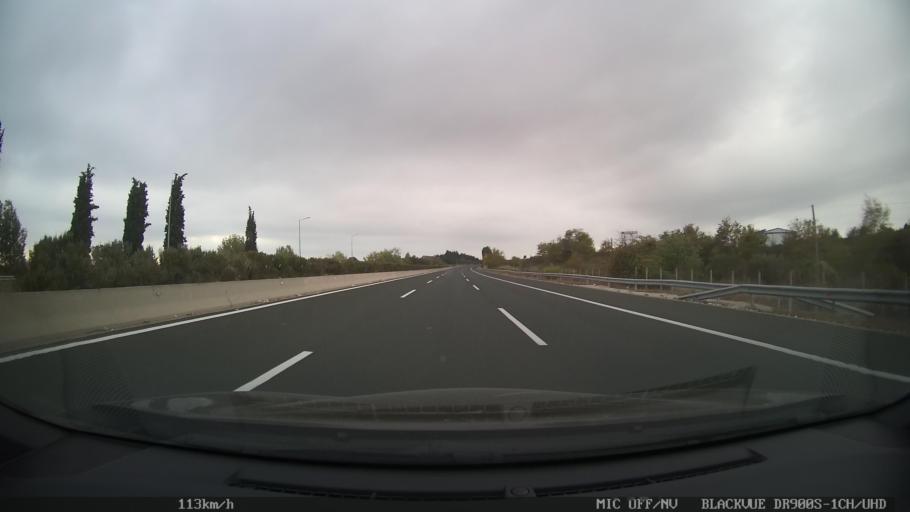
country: GR
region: Central Macedonia
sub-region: Nomos Pierias
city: Makrygialos
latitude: 40.3875
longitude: 22.6054
